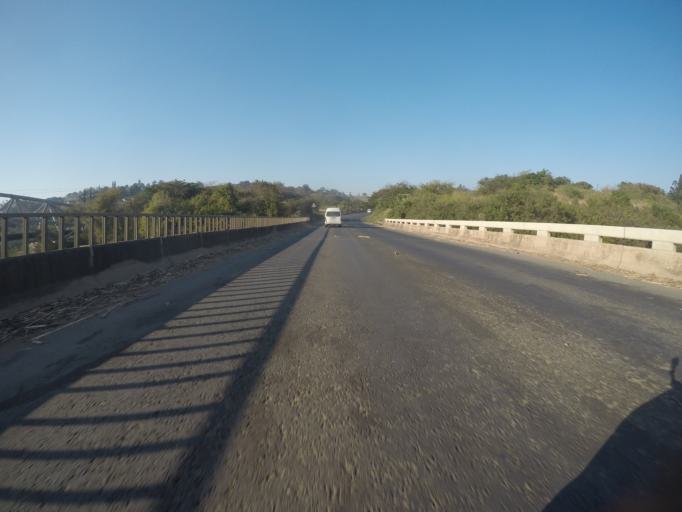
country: ZA
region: KwaZulu-Natal
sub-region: iLembe District Municipality
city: Stanger
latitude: -29.3840
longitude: 31.2533
